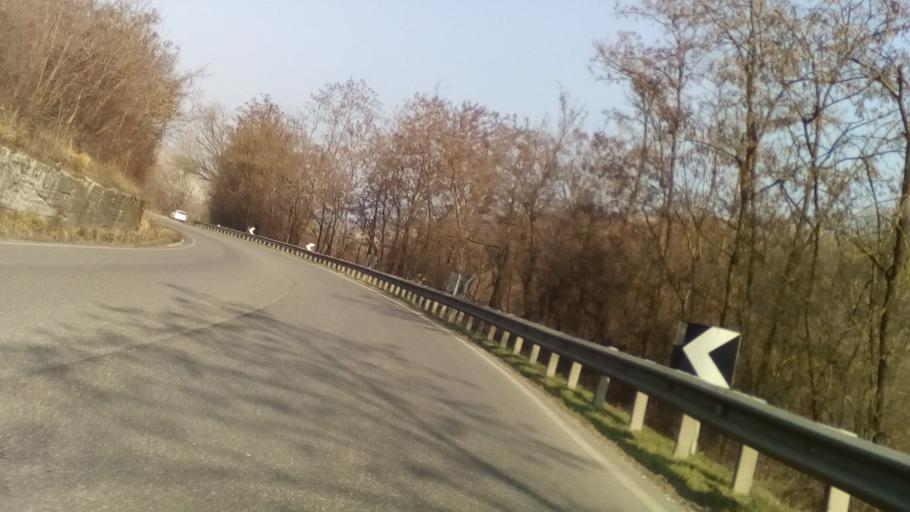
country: IT
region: Emilia-Romagna
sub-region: Provincia di Modena
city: Serramazzoni
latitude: 44.4630
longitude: 10.8367
